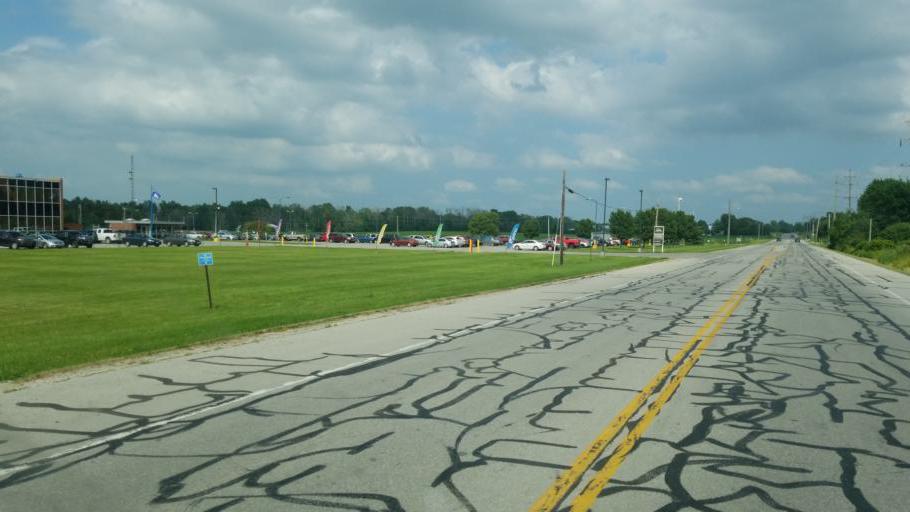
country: US
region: Ohio
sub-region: Crawford County
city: Crestline
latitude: 40.7864
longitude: -82.7006
